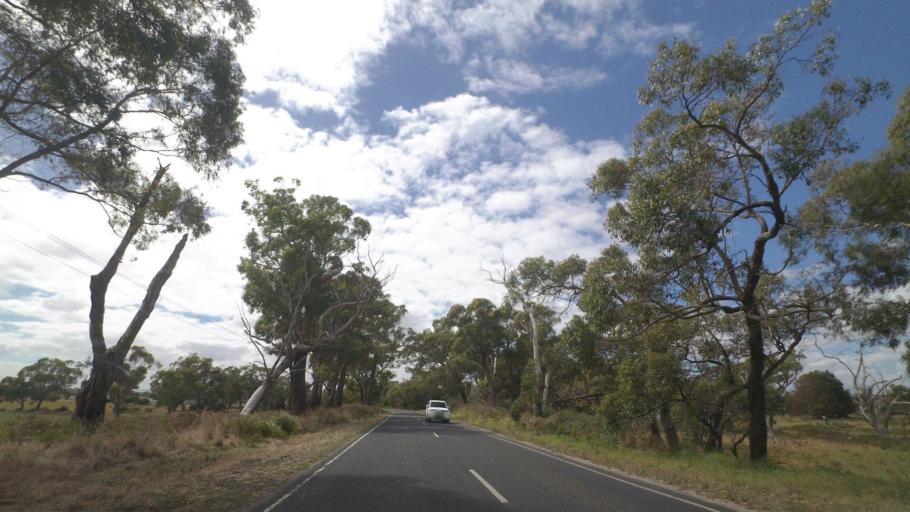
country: AU
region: Victoria
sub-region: Cardinia
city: Koo-Wee-Rup
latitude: -38.2825
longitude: 145.5940
